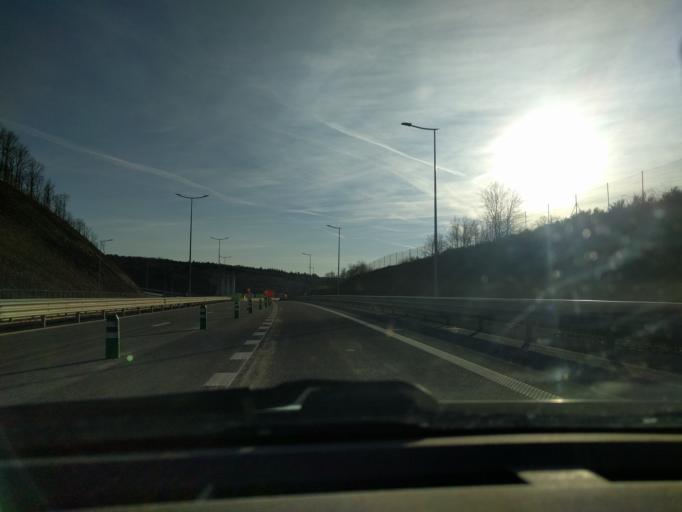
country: BE
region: Wallonia
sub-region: Province de Namur
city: Couvin
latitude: 50.0407
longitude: 4.5085
